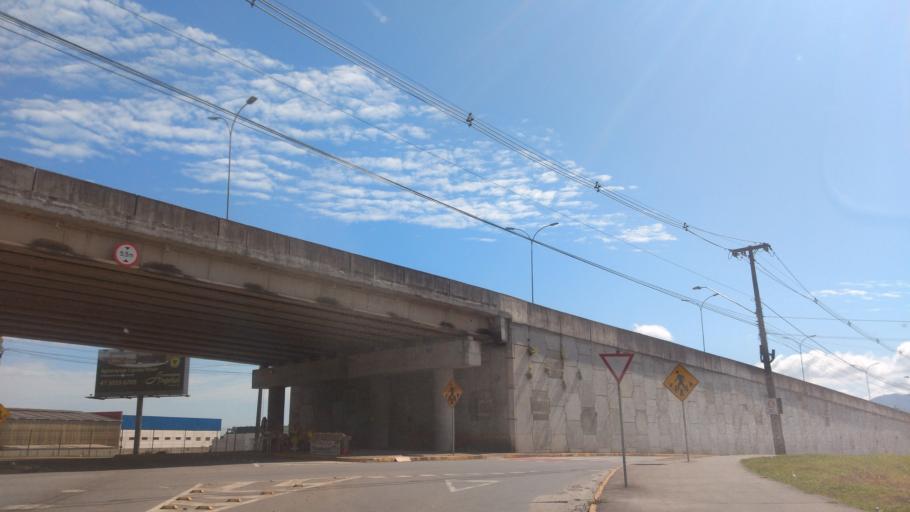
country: BR
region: Santa Catarina
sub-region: Joinville
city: Joinville
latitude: -26.2349
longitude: -48.8175
